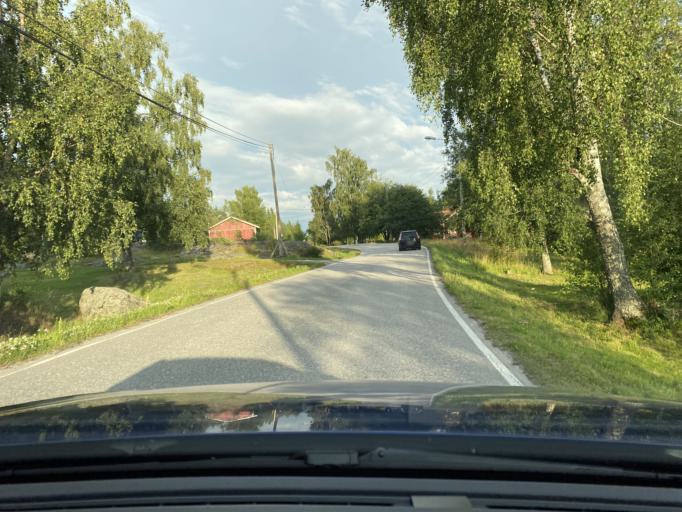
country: FI
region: Ostrobothnia
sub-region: Vaasa
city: Korsnaes
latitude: 62.9745
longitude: 21.1748
